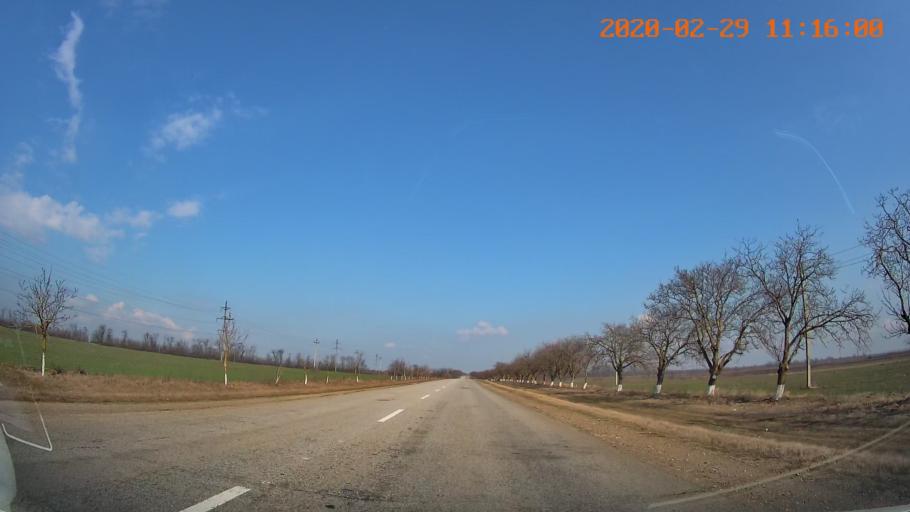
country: MD
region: Telenesti
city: Dubasari
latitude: 47.3028
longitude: 29.1671
